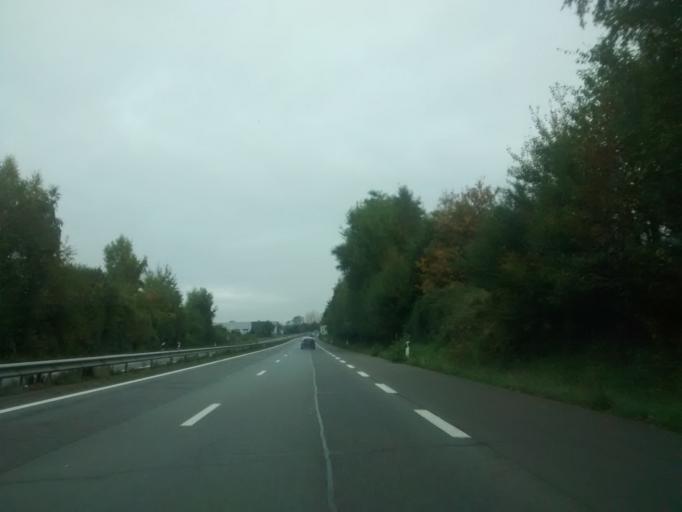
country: FR
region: Brittany
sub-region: Departement d'Ille-et-Vilaine
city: Miniac-Morvan
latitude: 48.5263
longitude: -1.9172
